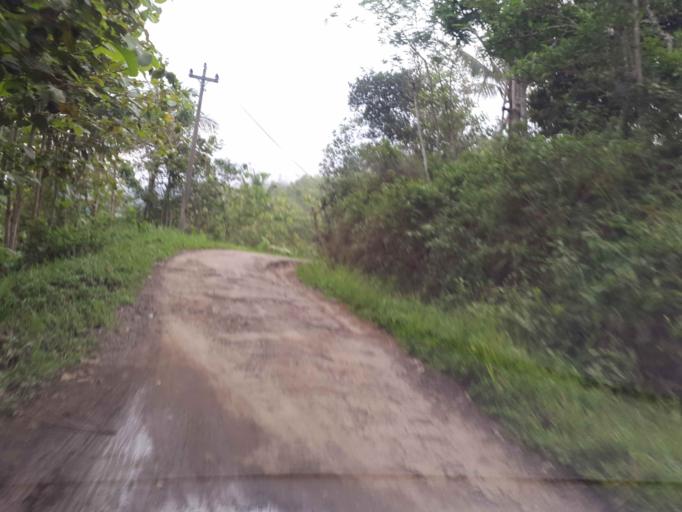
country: ID
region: Central Java
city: Genteng Wetan
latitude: -7.3643
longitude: 108.8946
